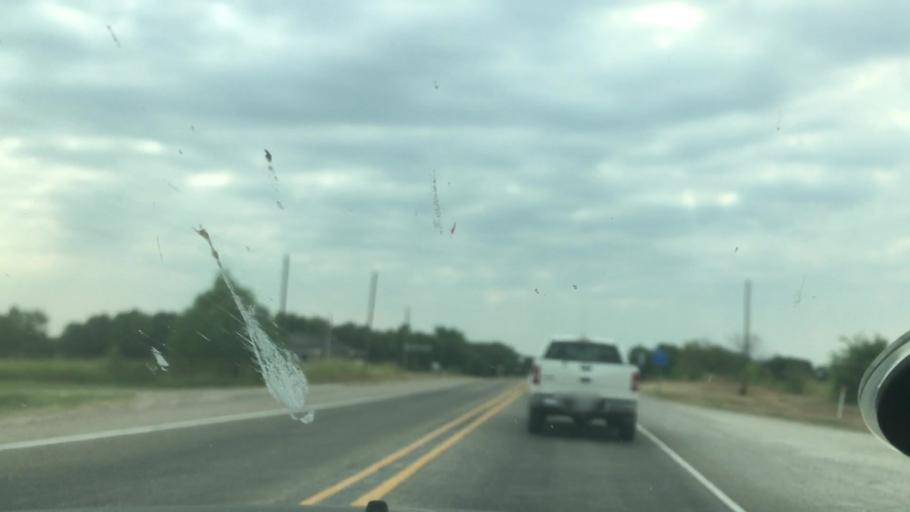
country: US
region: Texas
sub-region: Grayson County
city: Pottsboro
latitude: 33.8020
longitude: -96.6776
